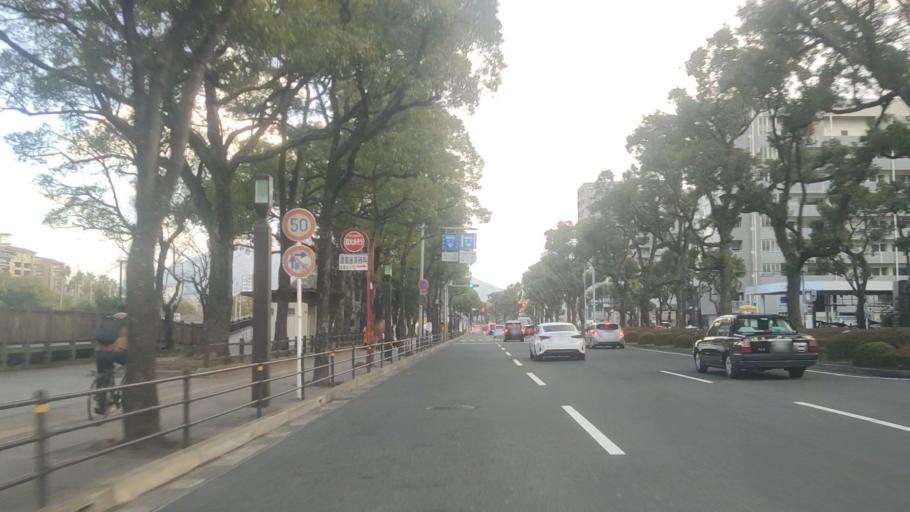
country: JP
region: Kagoshima
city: Kagoshima-shi
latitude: 31.5837
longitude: 130.5481
